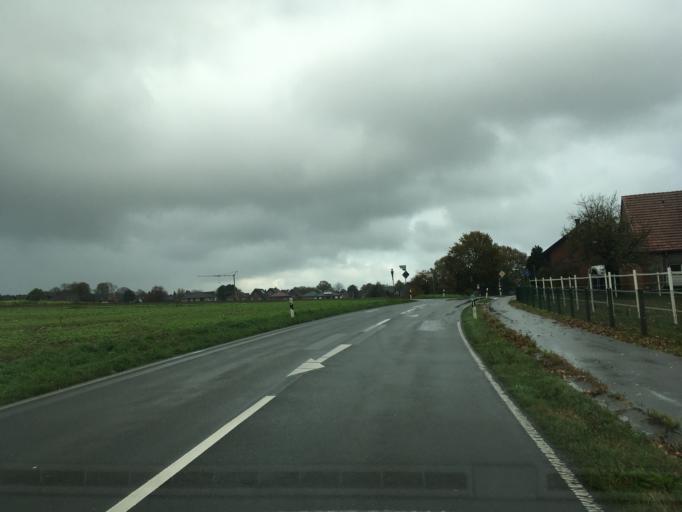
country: DE
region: North Rhine-Westphalia
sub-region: Regierungsbezirk Munster
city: Klein Reken
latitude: 51.8334
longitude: 7.0307
